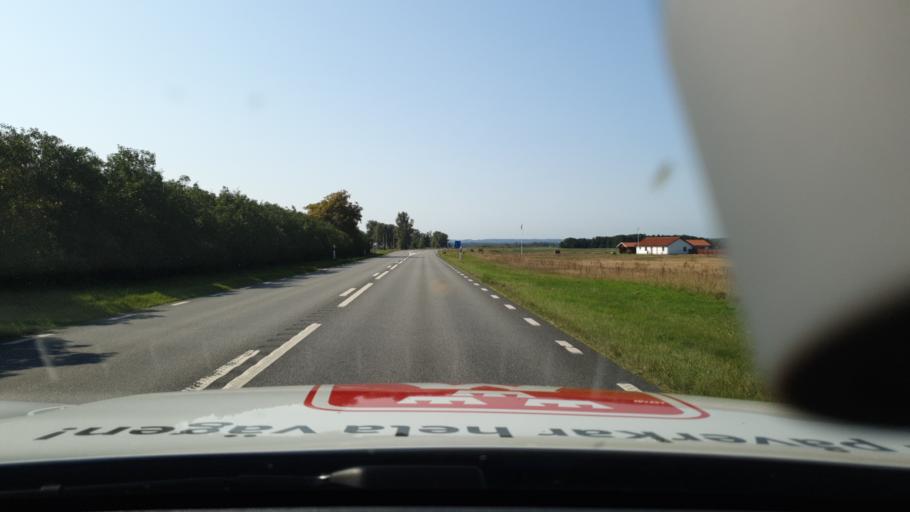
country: SE
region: Skane
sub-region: Kristianstads Kommun
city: Ahus
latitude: 55.8885
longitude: 14.2389
